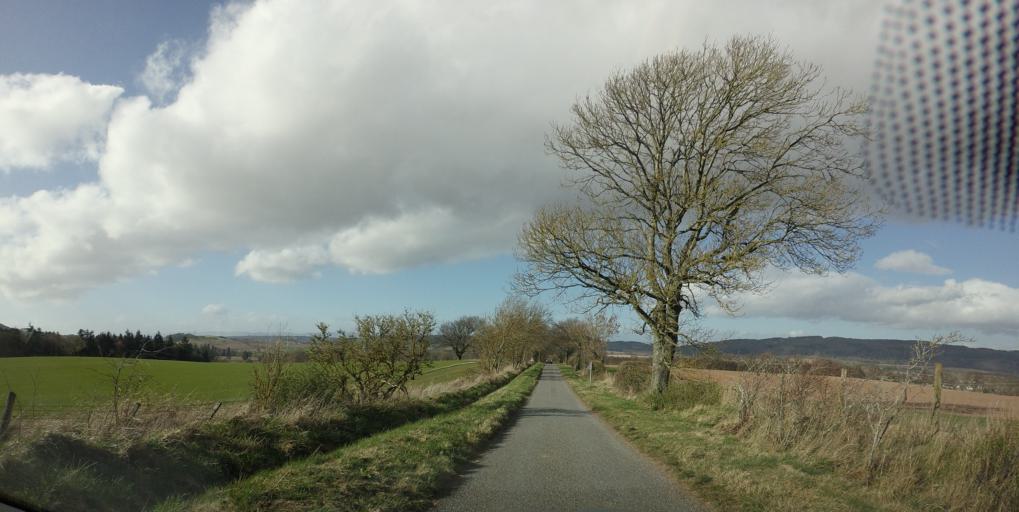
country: GB
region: Scotland
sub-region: Perth and Kinross
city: Bridge of Earn
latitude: 56.3281
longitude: -3.4154
